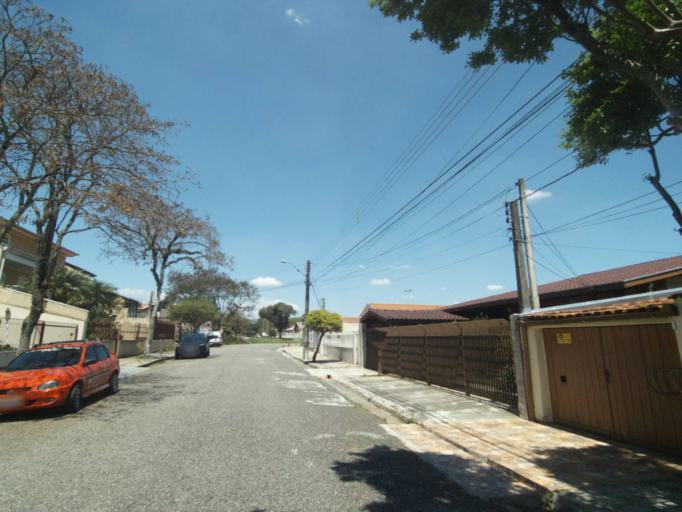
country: BR
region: Parana
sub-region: Pinhais
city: Pinhais
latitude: -25.3961
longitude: -49.2185
